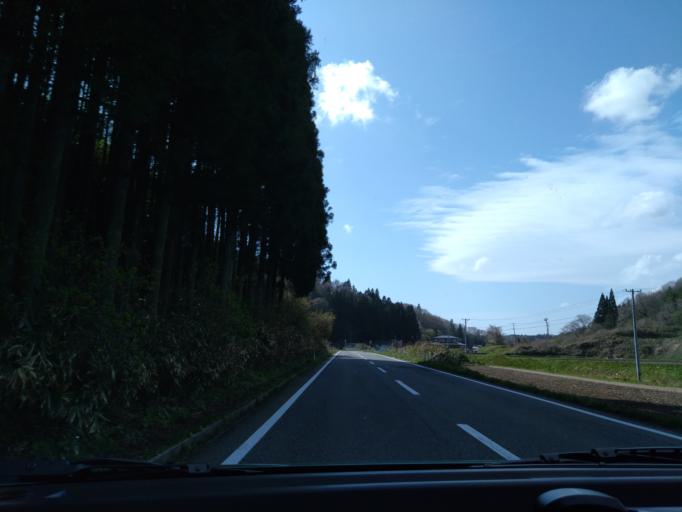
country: JP
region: Akita
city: Akita
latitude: 39.7066
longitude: 140.2094
